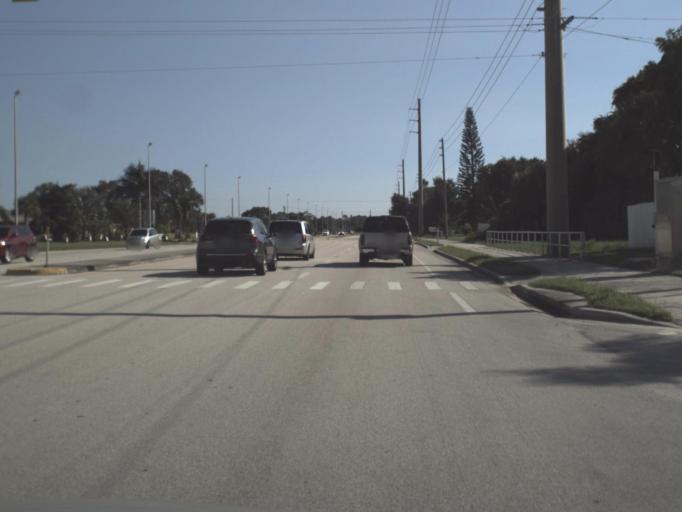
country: US
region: Florida
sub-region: Sarasota County
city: South Venice
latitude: 27.0359
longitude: -82.3980
